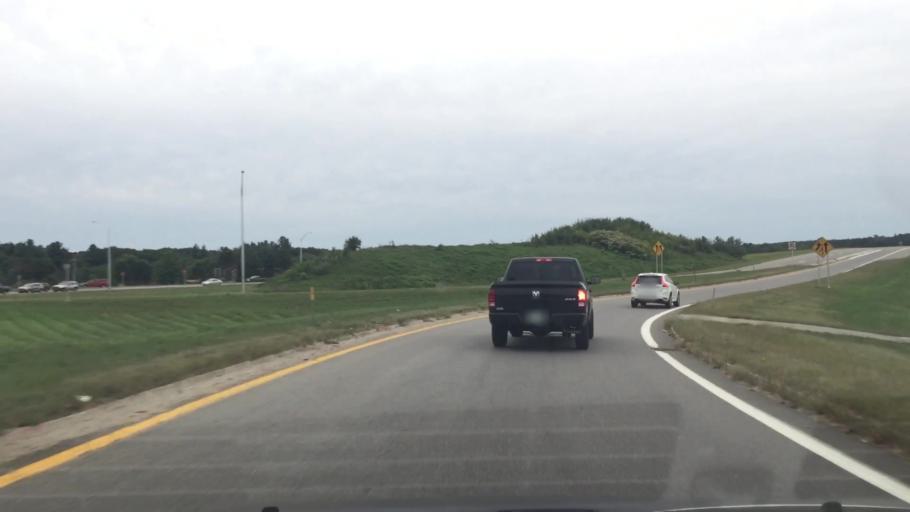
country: US
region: New Hampshire
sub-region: Hillsborough County
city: Hudson
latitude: 42.7301
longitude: -71.4255
